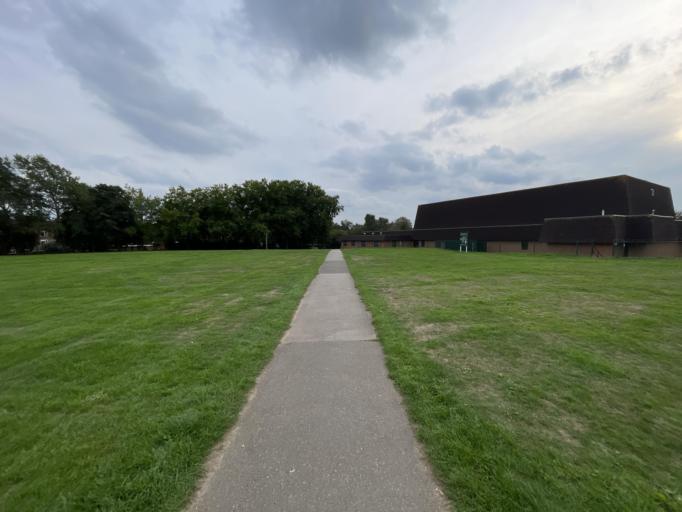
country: GB
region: England
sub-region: Hertfordshire
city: Hatfield
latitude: 51.7747
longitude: -0.2210
